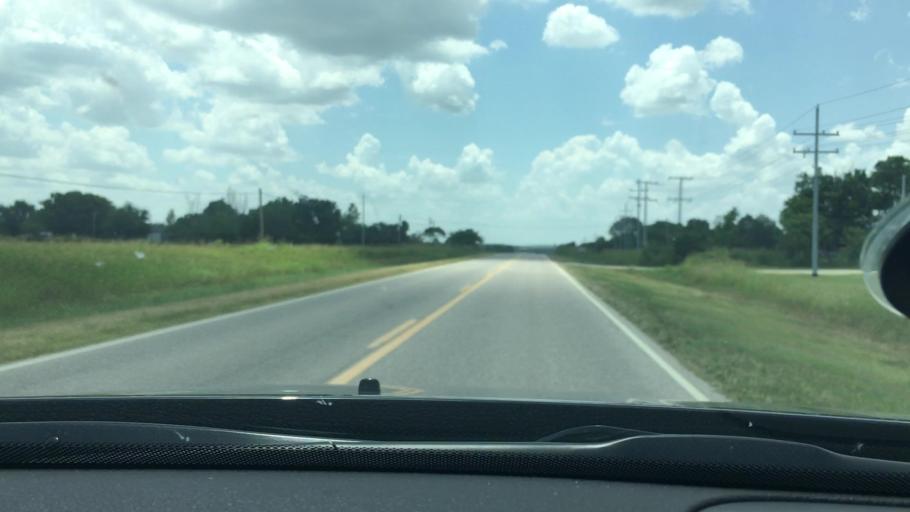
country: US
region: Oklahoma
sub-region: Pontotoc County
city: Ada
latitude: 34.6334
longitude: -96.6349
